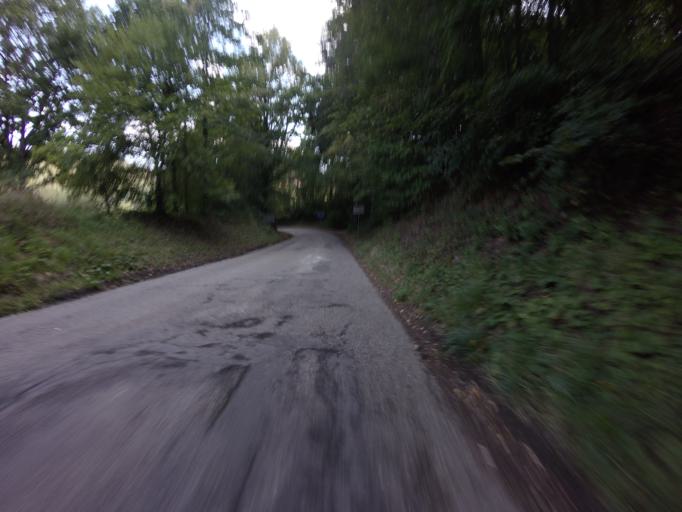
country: CZ
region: Jihocesky
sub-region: Okres Cesky Krumlov
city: Vyssi Brod
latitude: 48.6519
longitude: 14.3642
